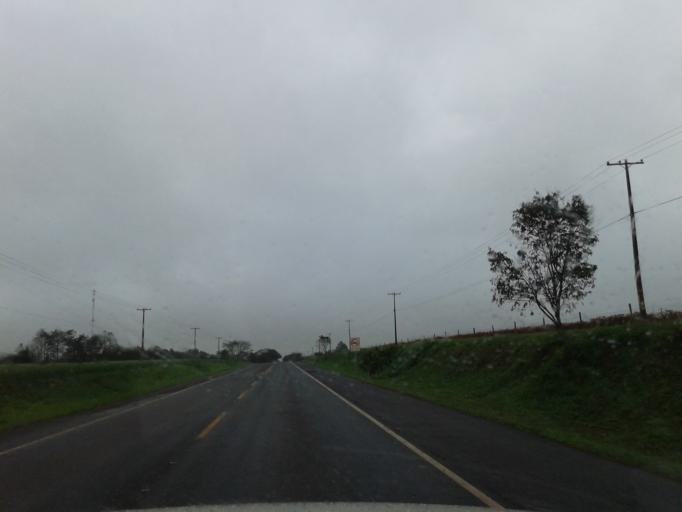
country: PY
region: Alto Parana
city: Naranjal
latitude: -26.1508
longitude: -55.1663
